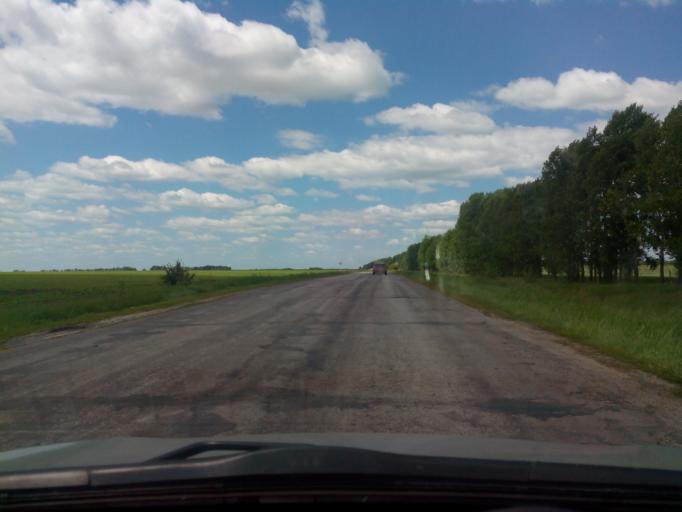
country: RU
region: Voronezj
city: Gribanovskiy
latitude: 51.6203
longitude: 41.9622
